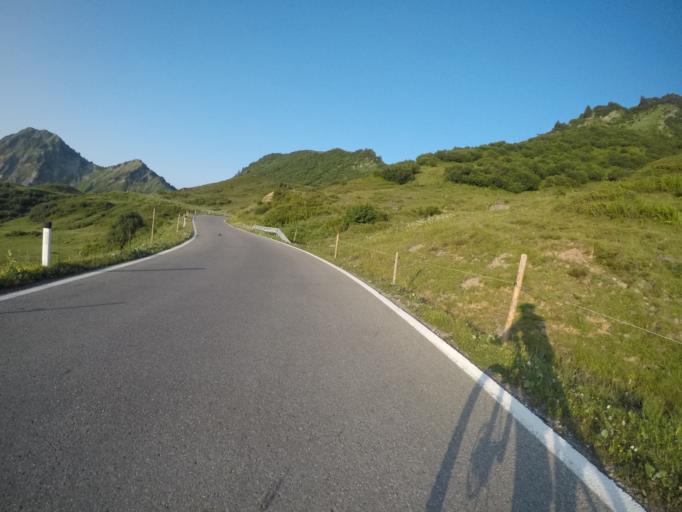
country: AT
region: Vorarlberg
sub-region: Politischer Bezirk Bludenz
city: Blons
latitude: 47.2747
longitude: 9.8349
